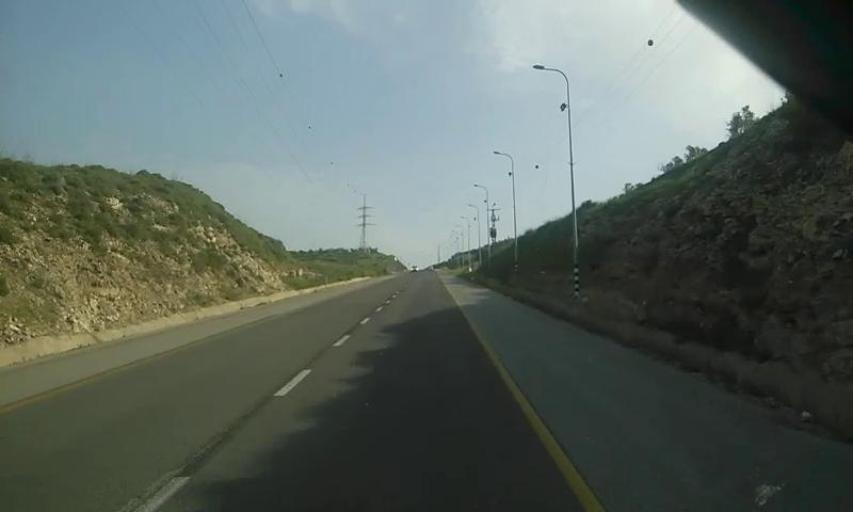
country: PS
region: West Bank
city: Sarrah
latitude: 32.2009
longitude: 35.1848
